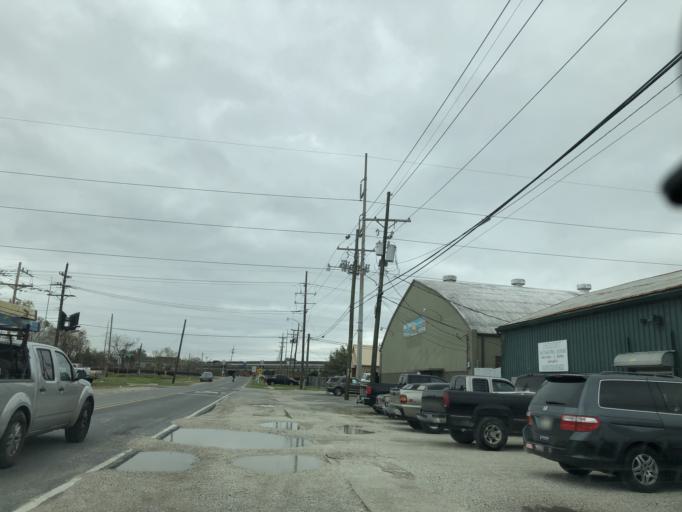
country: US
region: Louisiana
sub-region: Jefferson Parish
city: Metairie Terrace
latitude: 29.9733
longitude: -90.1608
